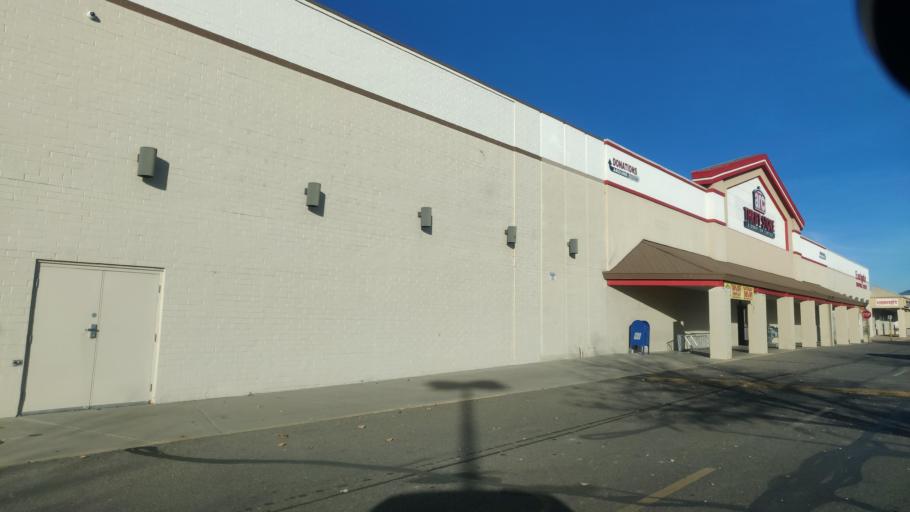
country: US
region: Colorado
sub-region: Mesa County
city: Grand Junction
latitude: 39.0783
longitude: -108.5277
